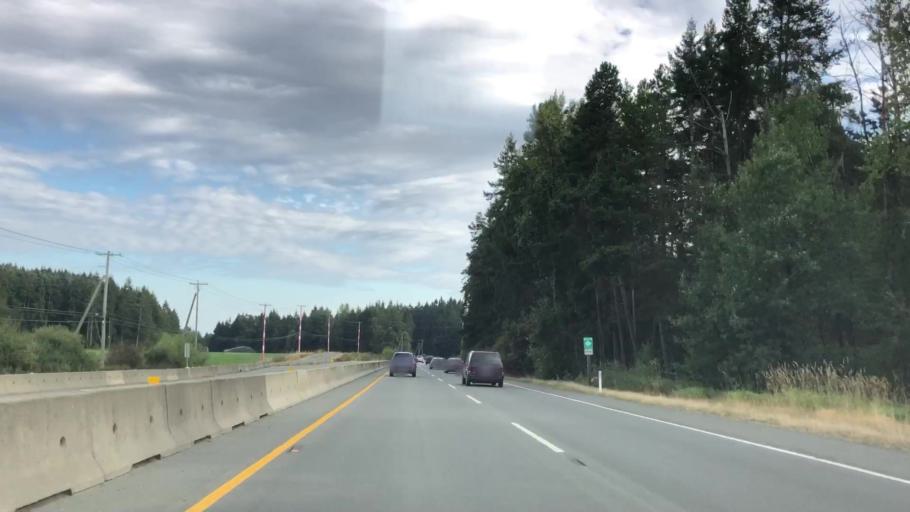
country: CA
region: British Columbia
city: Duncan
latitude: 48.7259
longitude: -123.6370
